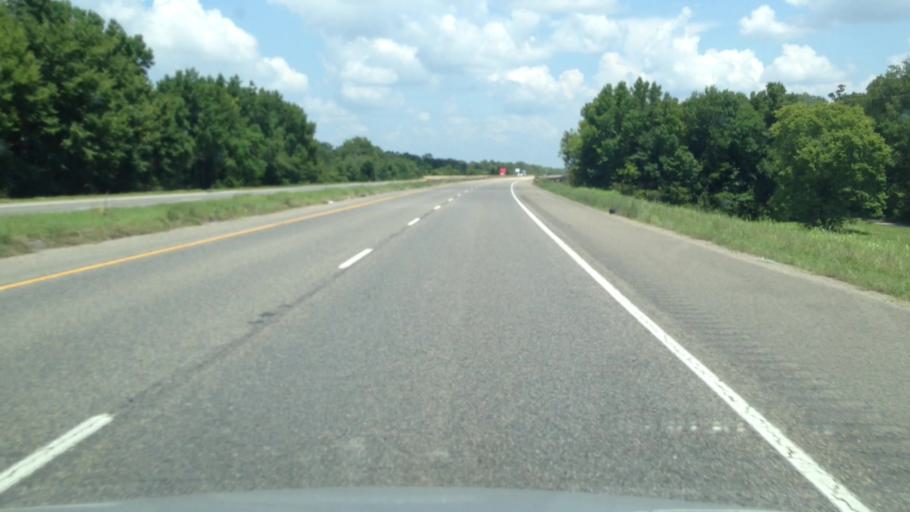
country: US
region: Louisiana
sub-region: Saint Landry Parish
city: Krotz Springs
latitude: 30.5487
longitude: -91.8354
